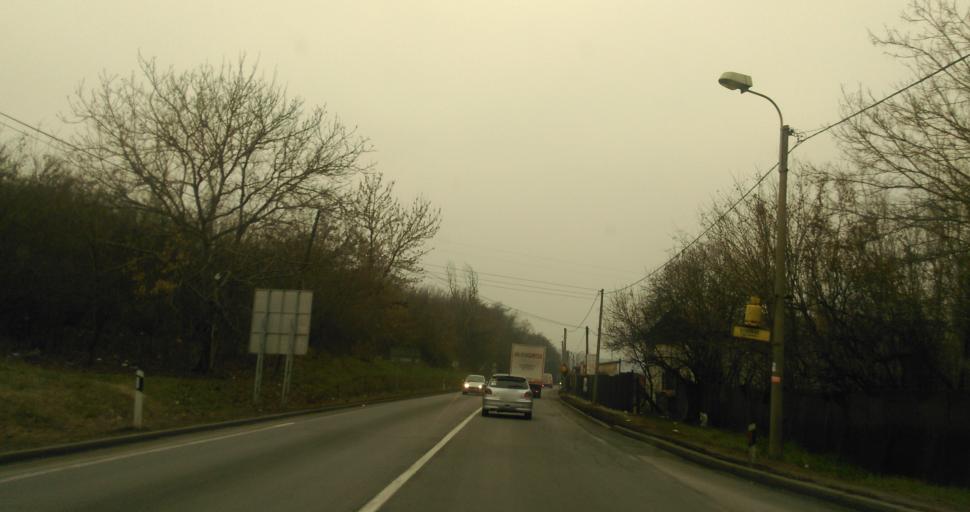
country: RS
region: Central Serbia
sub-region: Belgrade
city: Rakovica
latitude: 44.7174
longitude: 20.4654
